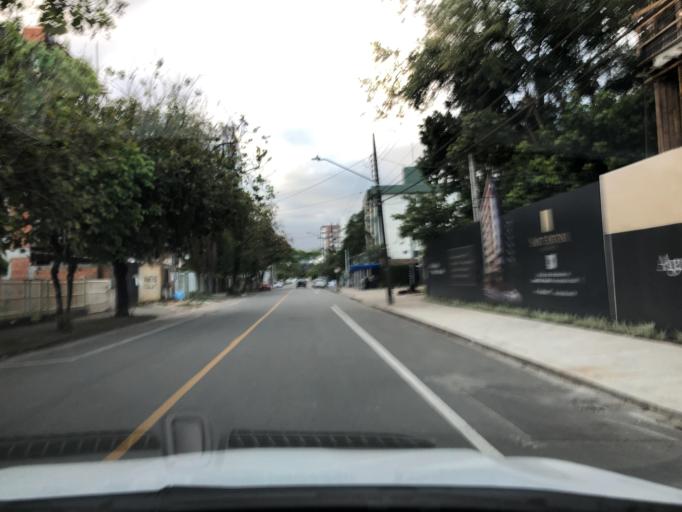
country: BR
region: Santa Catarina
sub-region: Joinville
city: Joinville
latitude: -26.2755
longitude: -48.8516
